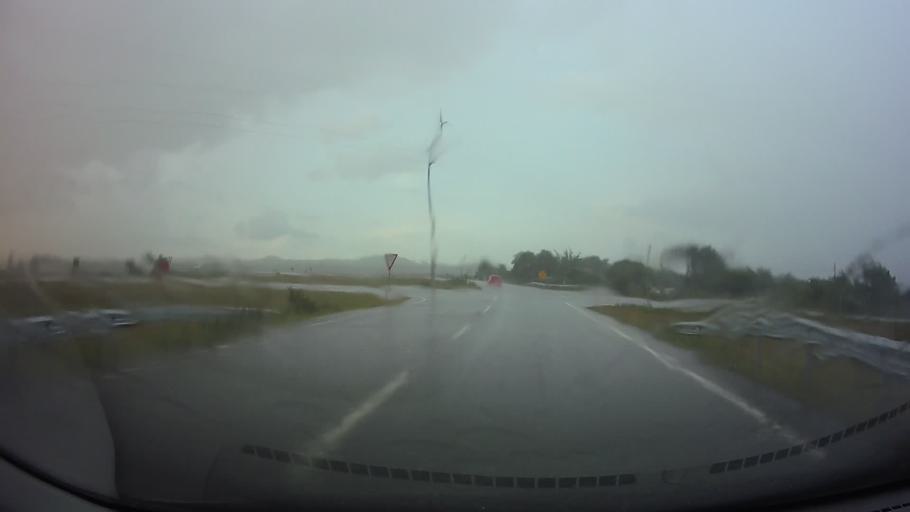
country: PY
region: Paraguari
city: Paraguari
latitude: -25.6358
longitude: -57.1541
